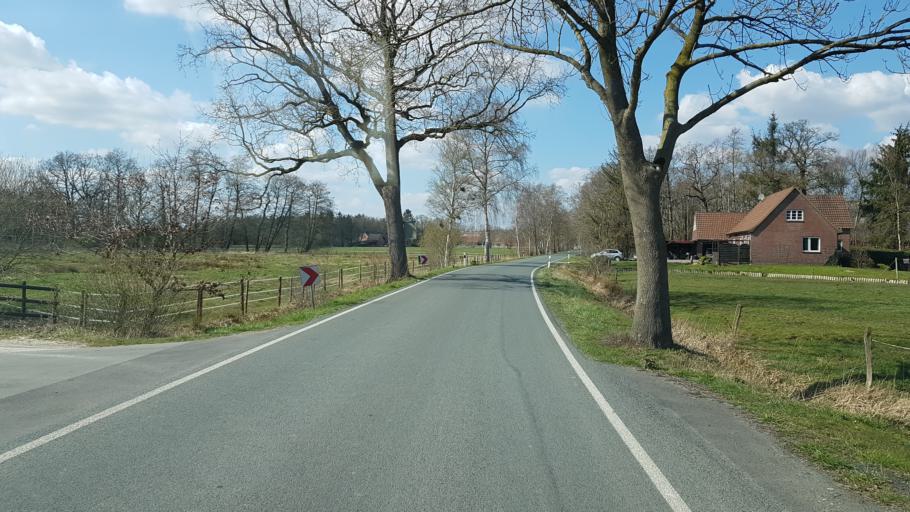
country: DE
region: Lower Saxony
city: Rastede
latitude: 53.3110
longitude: 8.2367
